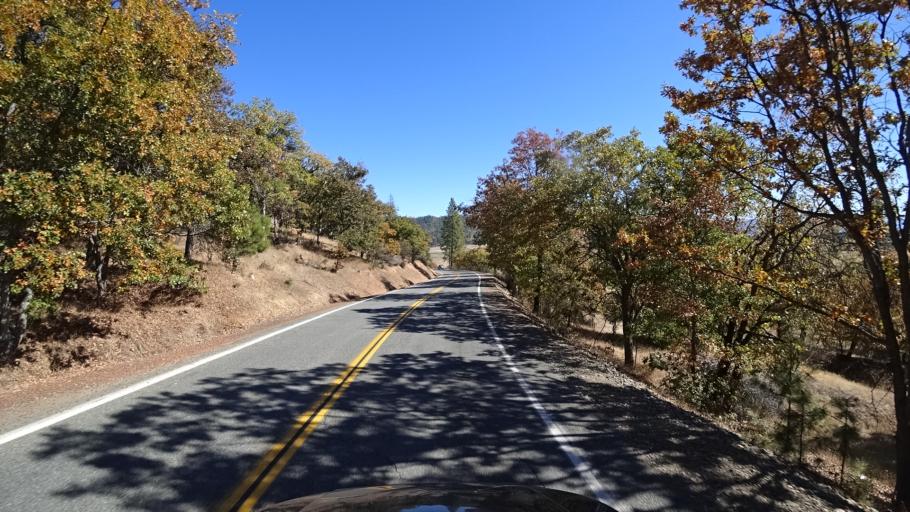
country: US
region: California
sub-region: Siskiyou County
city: Yreka
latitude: 41.5657
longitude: -122.9314
